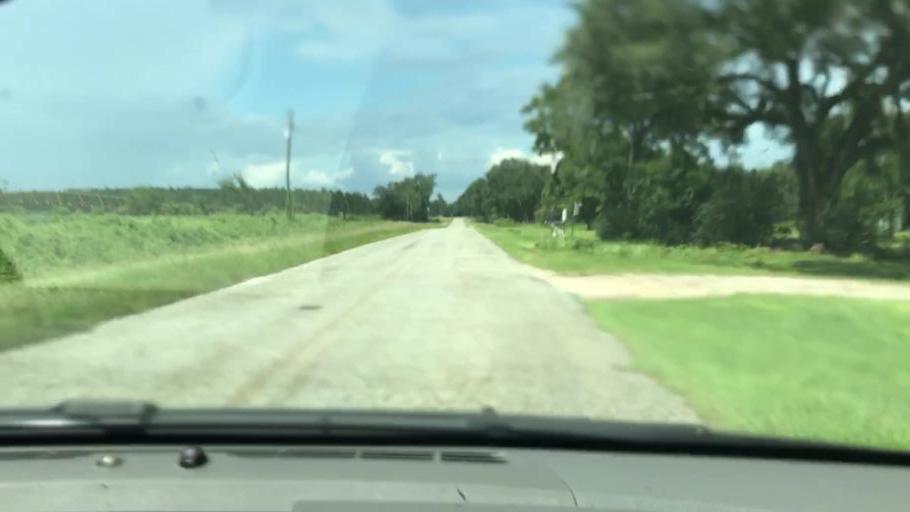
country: US
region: Georgia
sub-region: Early County
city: Blakely
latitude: 31.2147
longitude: -85.0032
